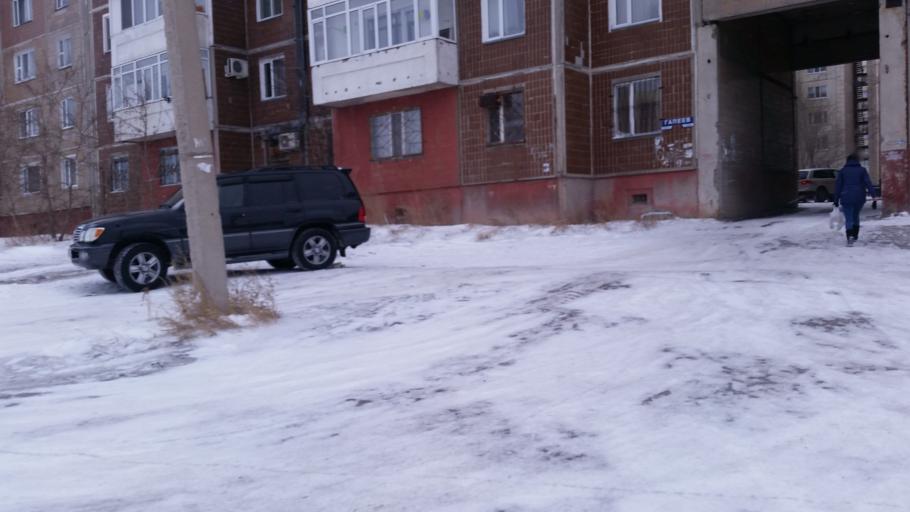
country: KZ
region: Qaraghandy
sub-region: Qaraghandy Qalasy
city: Karagandy
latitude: 49.7740
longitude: 73.1531
